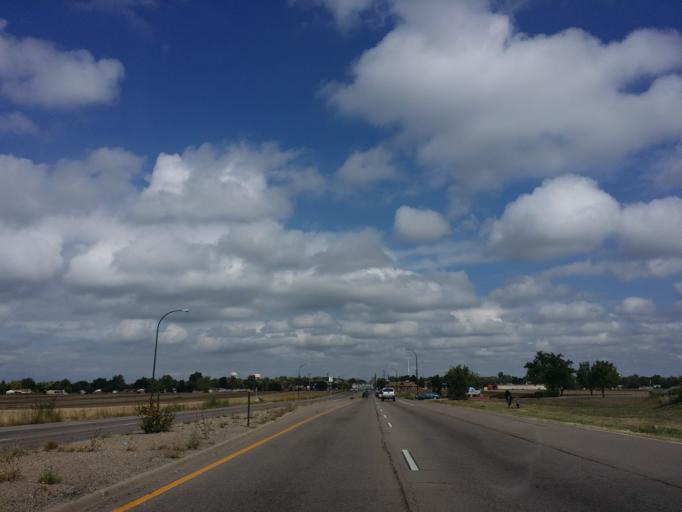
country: US
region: Colorado
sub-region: Adams County
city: Westminster
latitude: 39.8516
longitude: -105.0249
